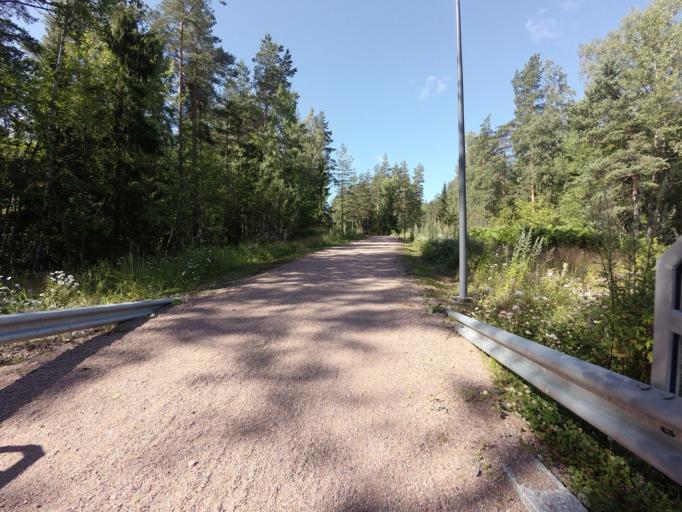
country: FI
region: Uusimaa
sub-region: Helsinki
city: Espoo
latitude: 60.1480
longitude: 24.5929
